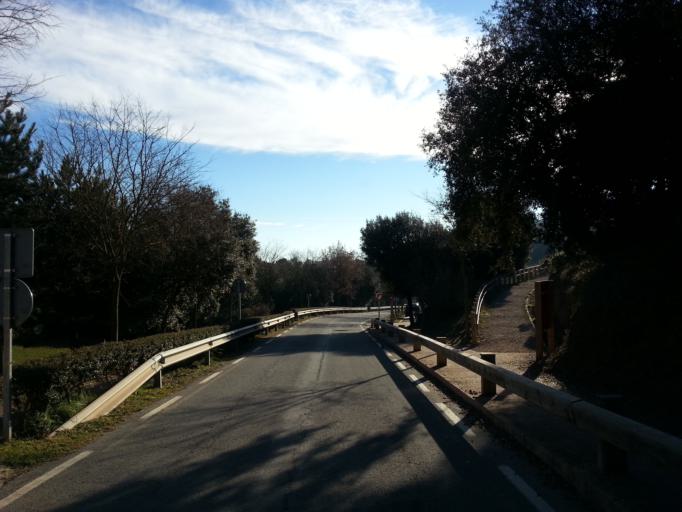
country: ES
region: Catalonia
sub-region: Provincia de Barcelona
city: Mura
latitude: 41.6698
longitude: 1.9947
